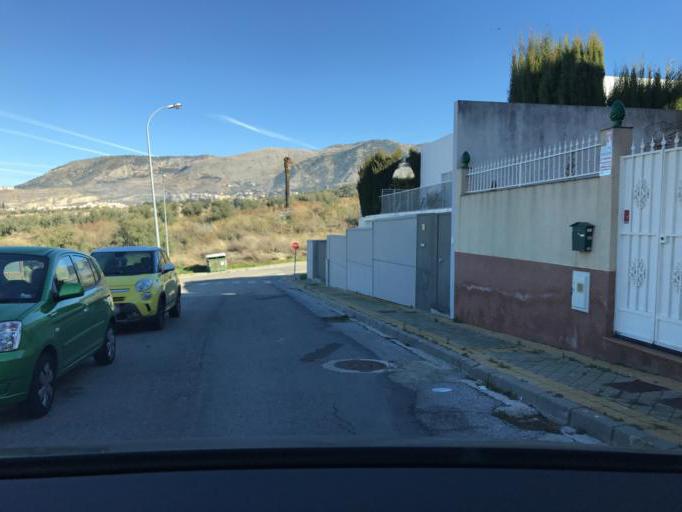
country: ES
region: Andalusia
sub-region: Provincia de Granada
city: Alfacar
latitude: 37.2198
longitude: -3.5726
